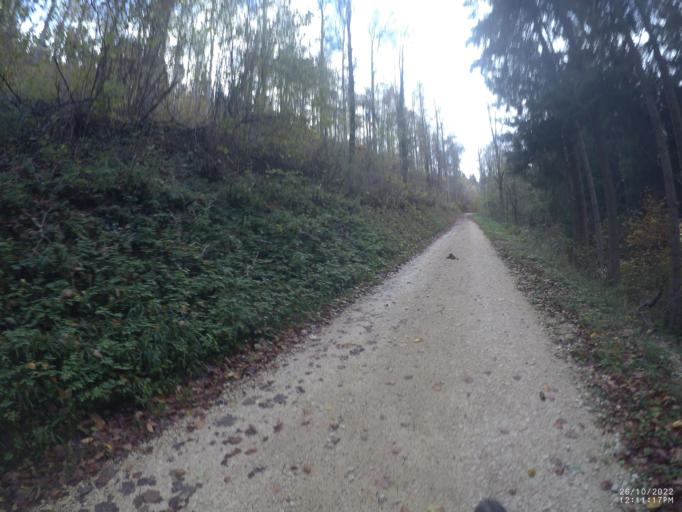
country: DE
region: Baden-Wuerttemberg
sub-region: Regierungsbezirk Stuttgart
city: Wiesensteig
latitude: 48.5451
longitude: 9.5991
